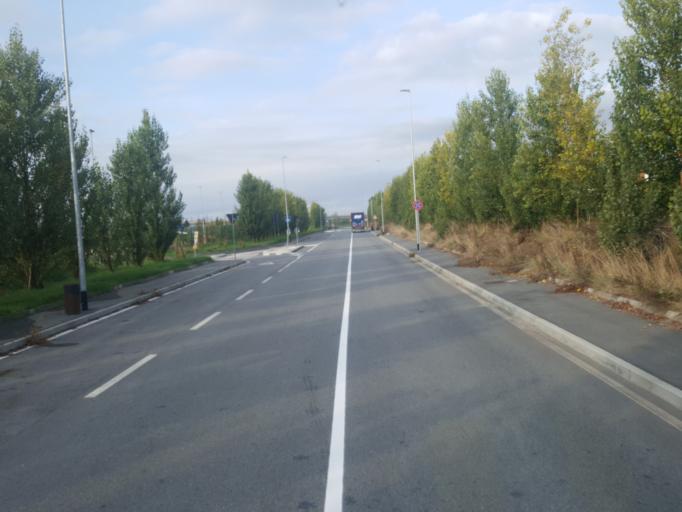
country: IT
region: Piedmont
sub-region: Provincia di Vercelli
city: Asigliano Vercellese
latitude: 45.2925
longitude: 8.3947
